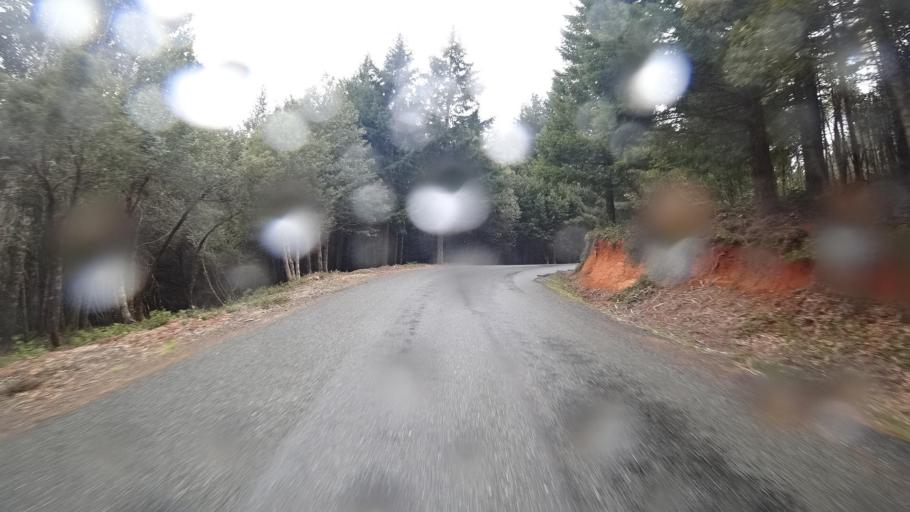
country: US
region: California
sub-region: Humboldt County
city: Willow Creek
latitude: 41.2011
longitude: -123.7949
